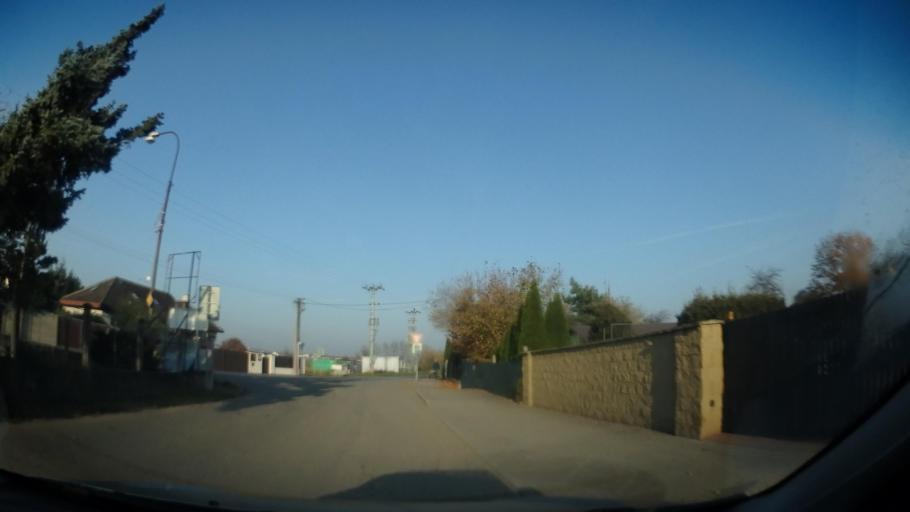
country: CZ
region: Central Bohemia
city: Jirny
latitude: 50.1072
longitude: 14.7067
